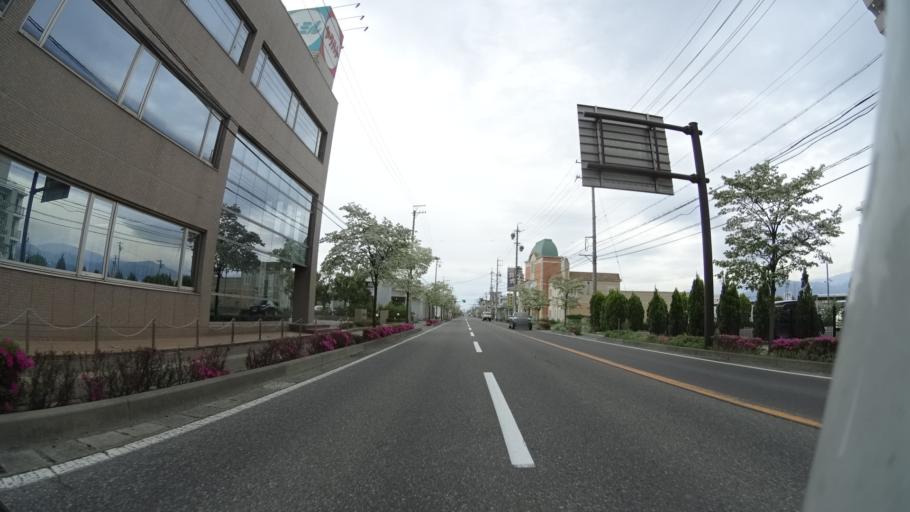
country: JP
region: Nagano
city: Nagano-shi
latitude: 36.6065
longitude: 138.1646
